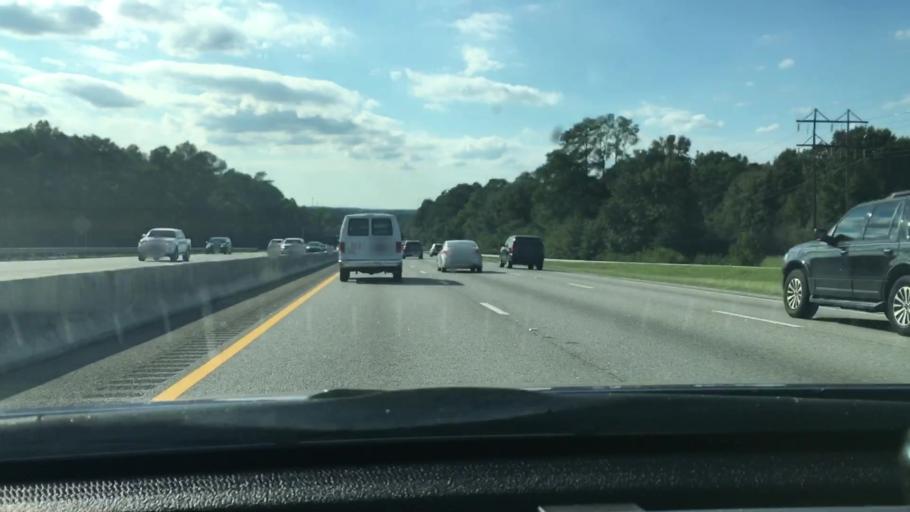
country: US
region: South Carolina
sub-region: Richland County
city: Dentsville
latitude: 34.0732
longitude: -80.9800
